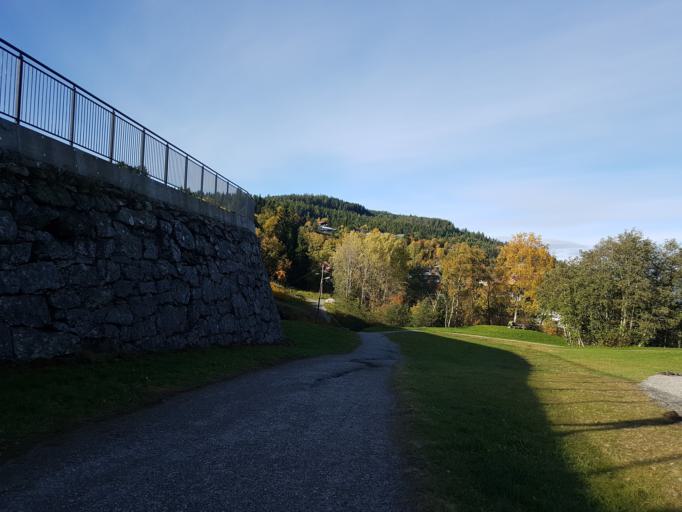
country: NO
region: Sor-Trondelag
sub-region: Trondheim
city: Trondheim
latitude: 63.4230
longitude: 10.3492
